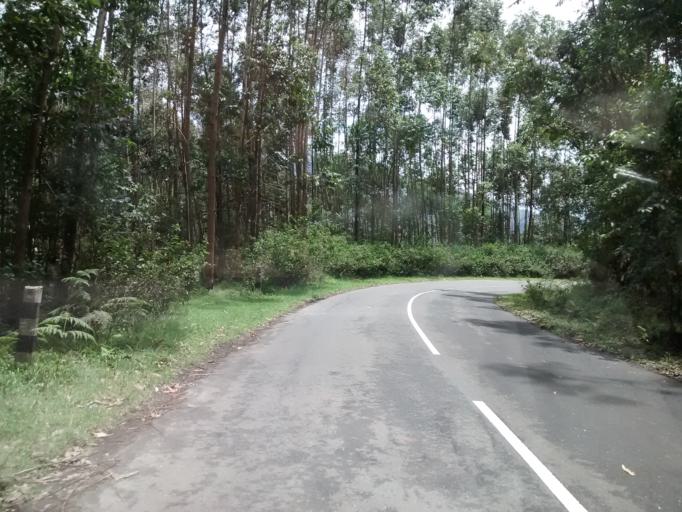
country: IN
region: Kerala
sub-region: Idukki
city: Munnar
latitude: 10.1243
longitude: 77.1583
